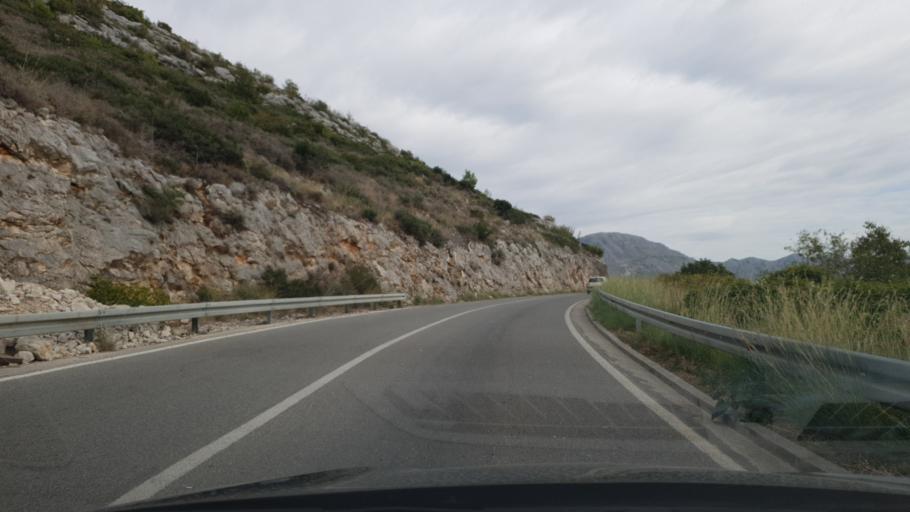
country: HR
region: Dubrovacko-Neretvanska
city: Cibaca
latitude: 42.6383
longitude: 18.1627
